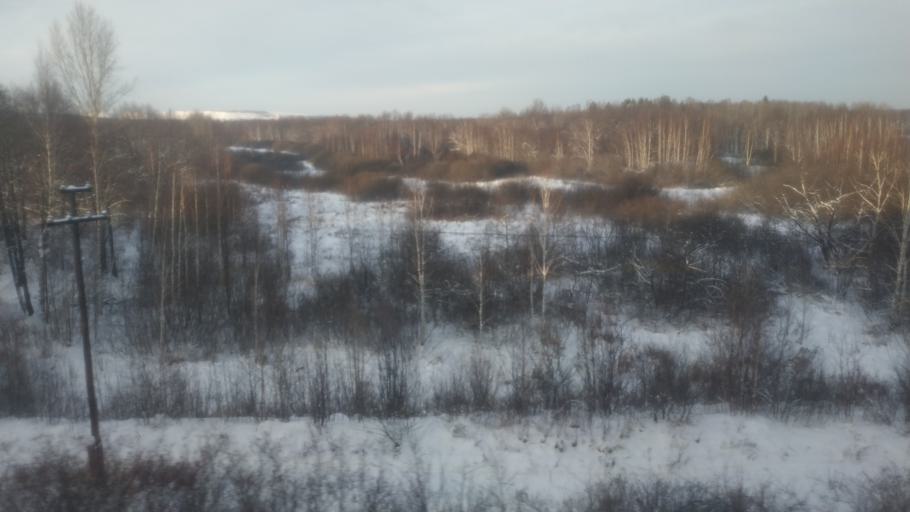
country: RU
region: Kirov
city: Vyatskiye Polyany
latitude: 56.2565
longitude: 51.0865
